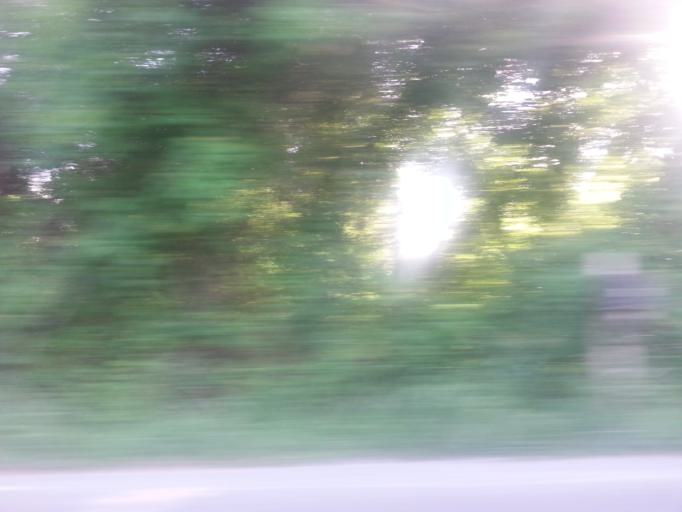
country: US
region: Tennessee
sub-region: Blount County
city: Wildwood
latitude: 35.8812
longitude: -83.8978
